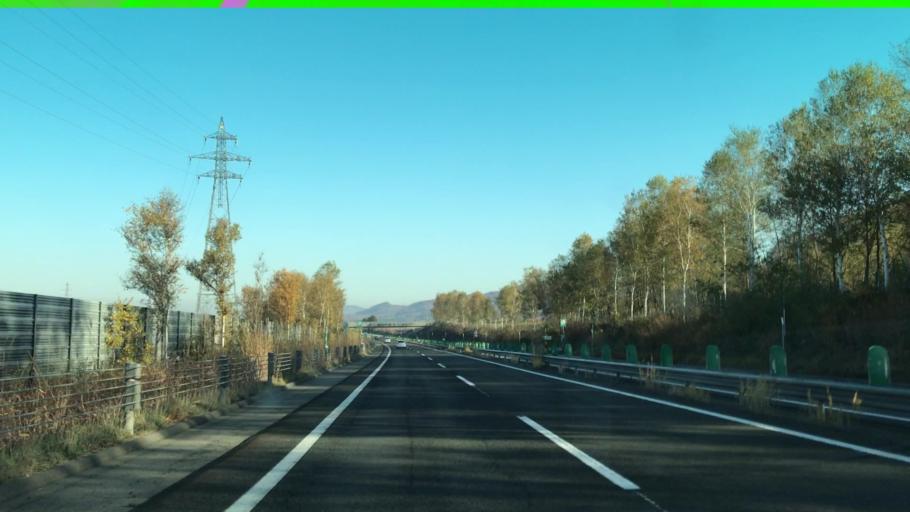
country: JP
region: Hokkaido
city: Sunagawa
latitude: 43.4292
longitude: 141.9137
